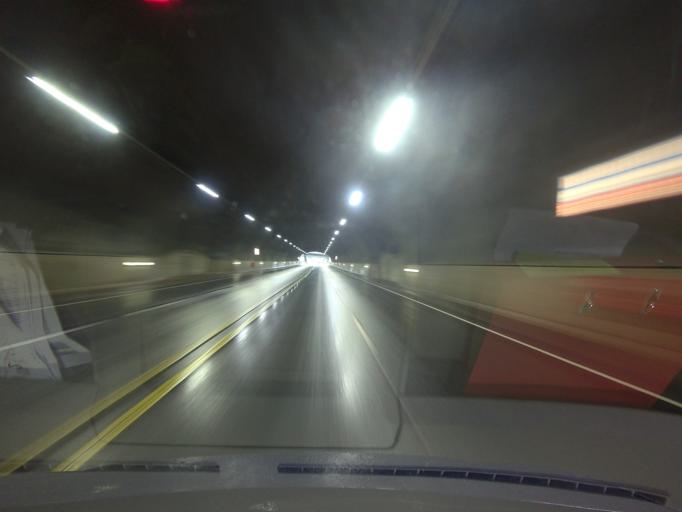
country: FI
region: Uusimaa
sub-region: Helsinki
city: Kauniainen
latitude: 60.2123
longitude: 24.7473
